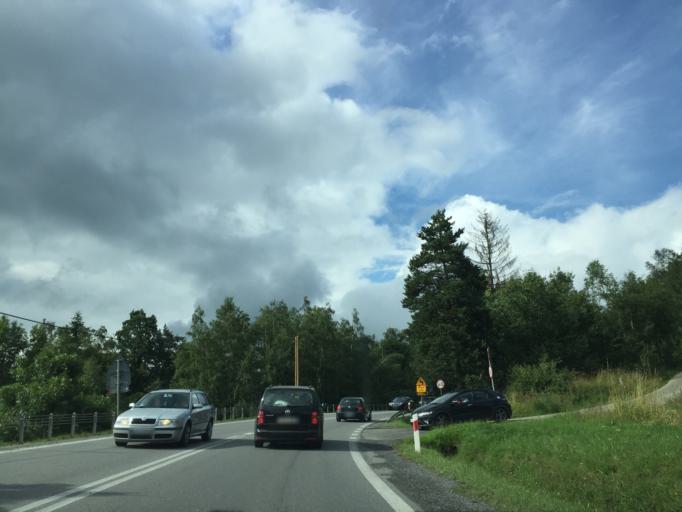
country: PL
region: Lesser Poland Voivodeship
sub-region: Powiat suski
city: Naprawa
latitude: 49.6548
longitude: 19.9014
